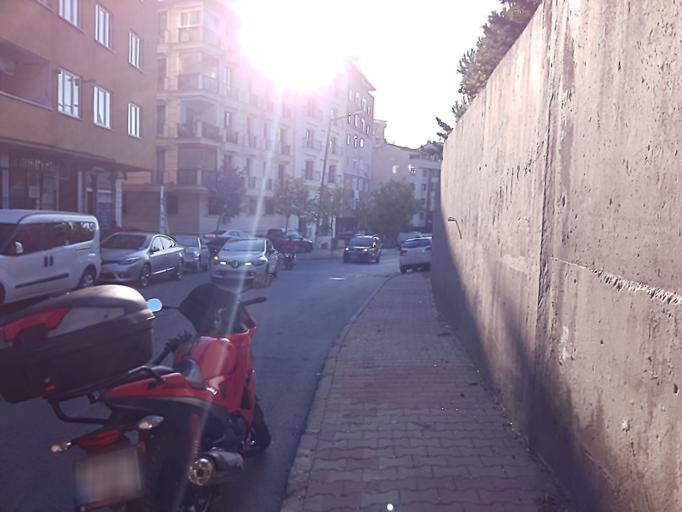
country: TR
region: Istanbul
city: Sisli
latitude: 41.0716
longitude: 29.0051
